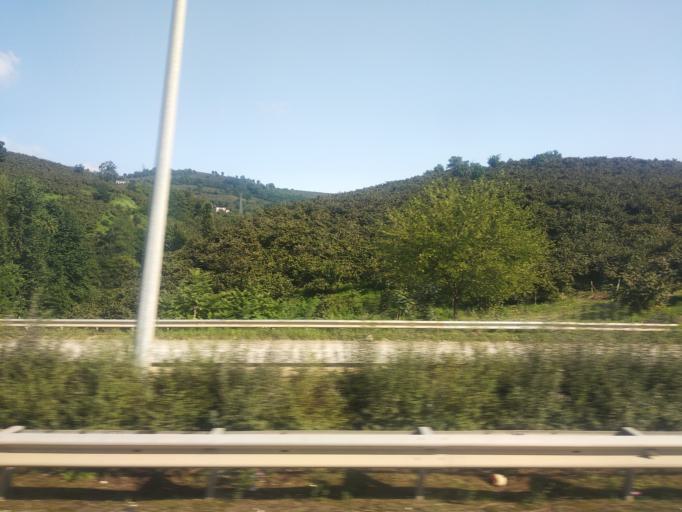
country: TR
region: Ordu
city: Ordu
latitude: 40.9946
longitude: 37.8177
